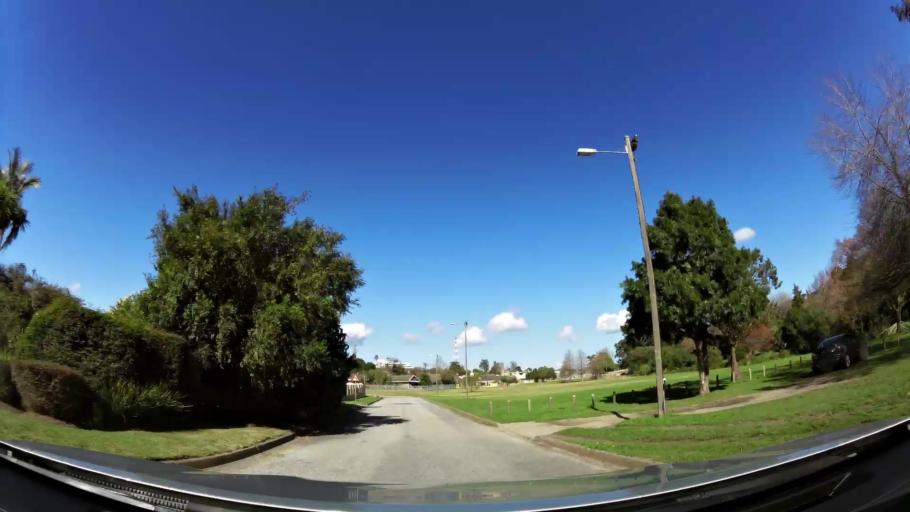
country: ZA
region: Western Cape
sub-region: Eden District Municipality
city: George
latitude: -33.9510
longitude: 22.4564
